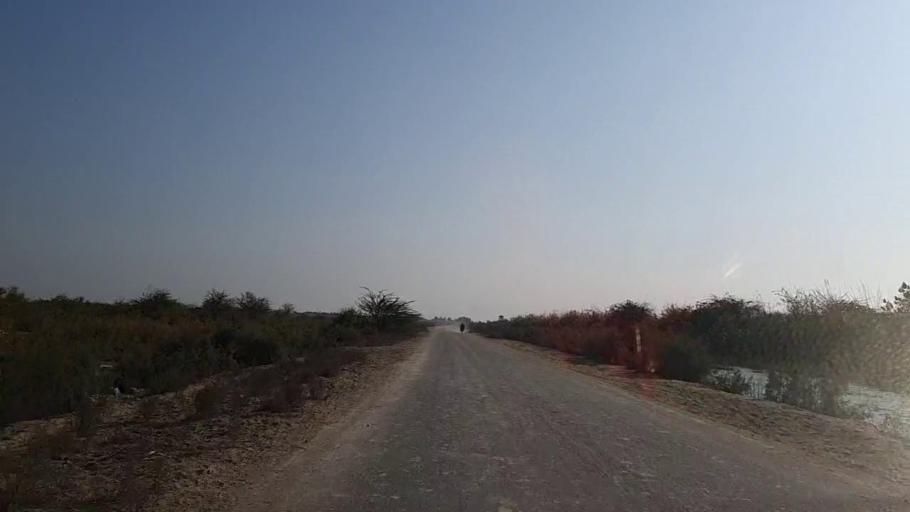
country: PK
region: Sindh
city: Tando Mittha Khan
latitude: 25.9095
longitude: 69.0762
